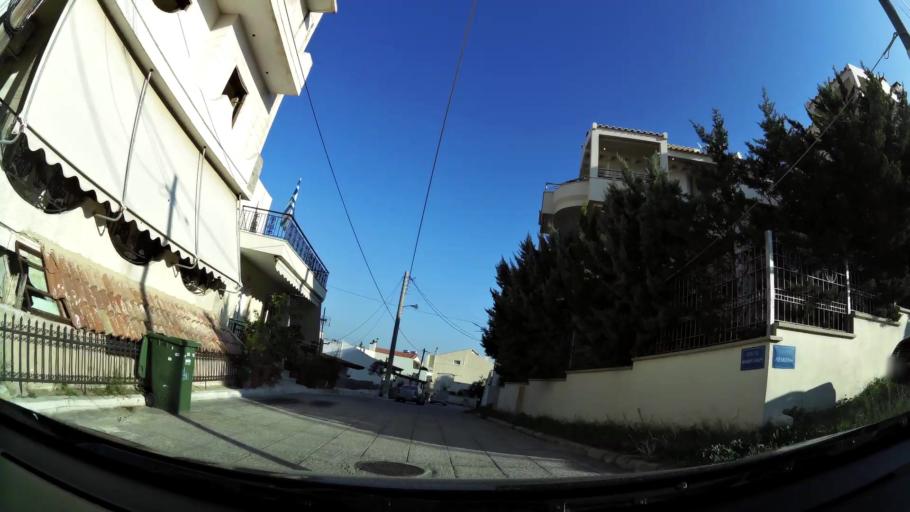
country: GR
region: Attica
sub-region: Nomos Piraios
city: Korydallos
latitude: 37.9746
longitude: 23.6335
